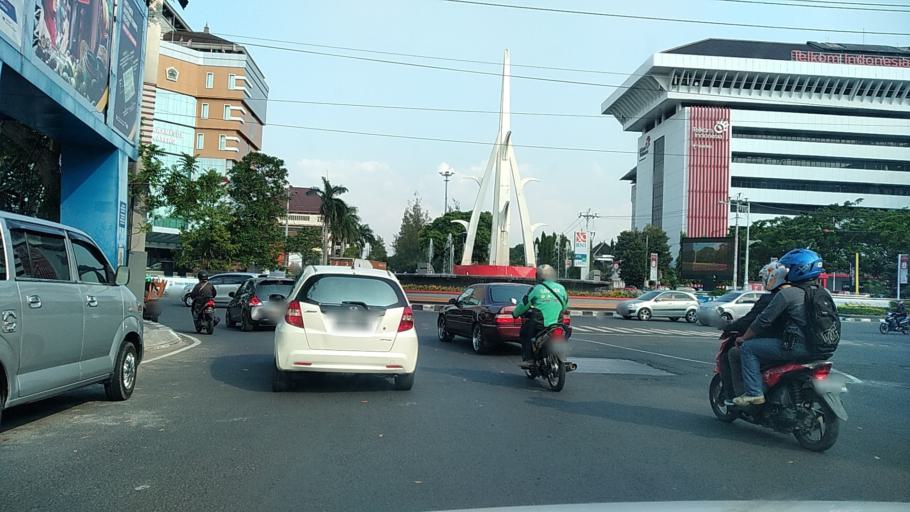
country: ID
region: Central Java
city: Semarang
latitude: -6.9929
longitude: 110.4211
